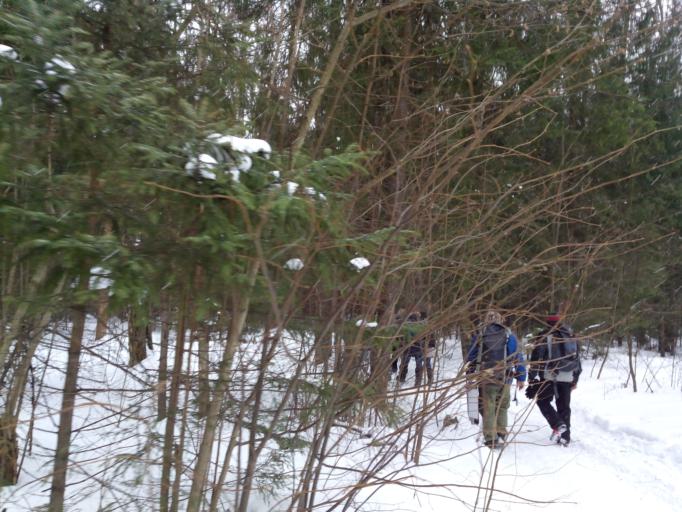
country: RU
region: Moskovskaya
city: Bol'shiye Vyazemy
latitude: 55.6668
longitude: 36.9756
